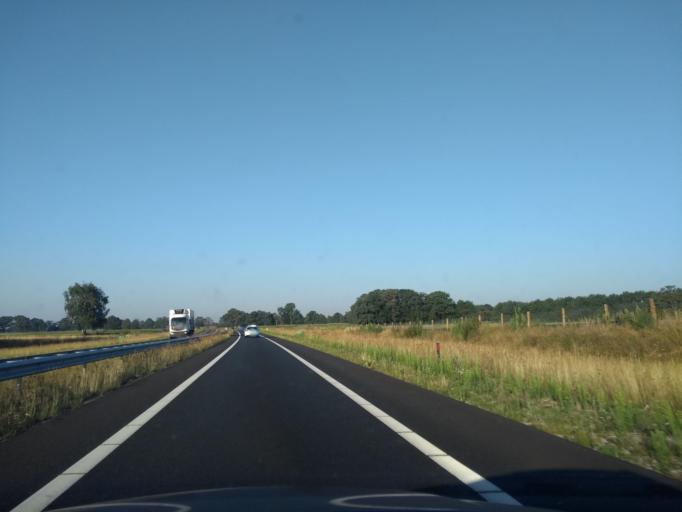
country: NL
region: Overijssel
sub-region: Gemeente Haaksbergen
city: Haaksbergen
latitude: 52.1768
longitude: 6.7211
